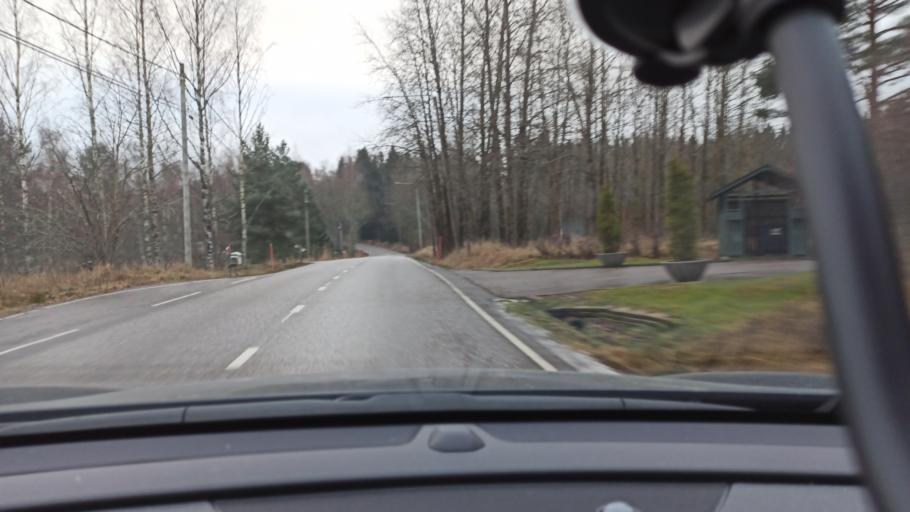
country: FI
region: Uusimaa
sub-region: Helsinki
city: Kirkkonummi
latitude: 60.1505
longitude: 24.4606
